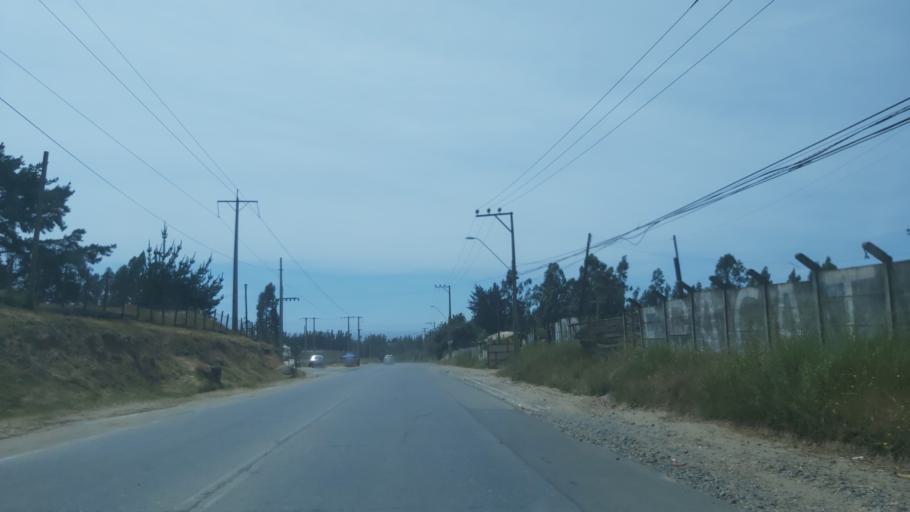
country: CL
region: Maule
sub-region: Provincia de Talca
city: Constitucion
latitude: -35.3618
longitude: -72.4047
